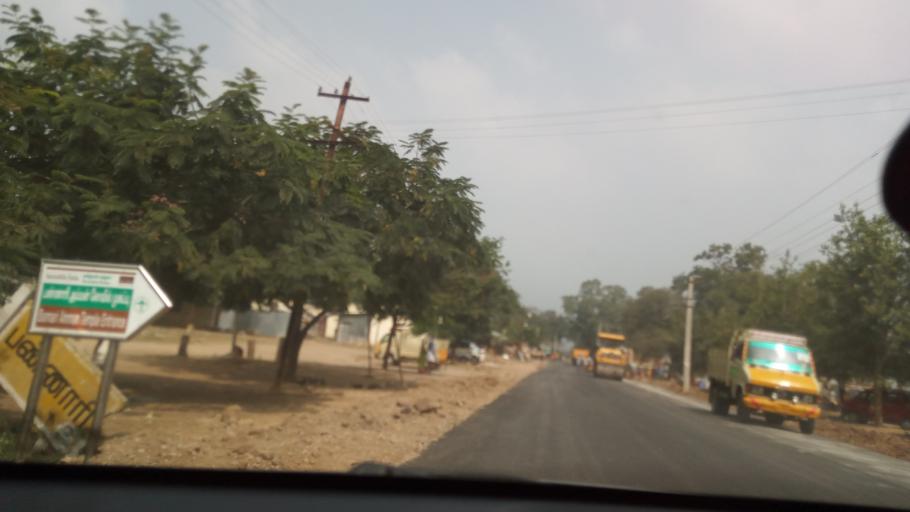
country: IN
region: Tamil Nadu
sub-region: Erode
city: Sathyamangalam
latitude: 11.5512
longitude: 77.1388
